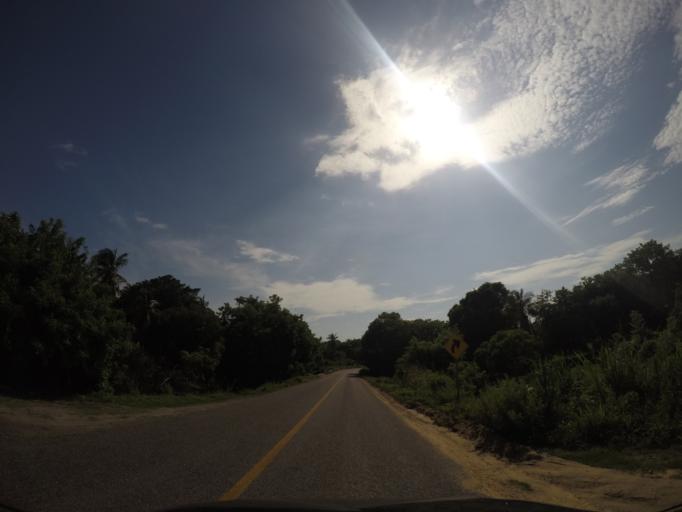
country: MX
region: Oaxaca
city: San Pedro Mixtepec
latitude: 15.9394
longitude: -97.1624
